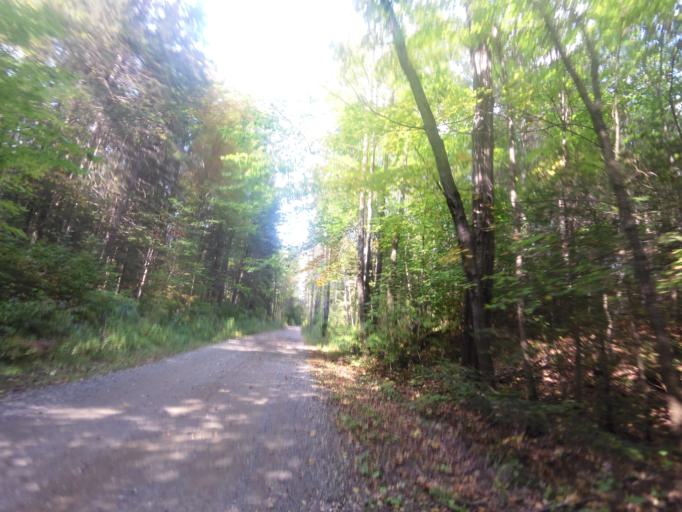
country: CA
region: Ontario
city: Renfrew
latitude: 45.1410
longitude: -76.6865
